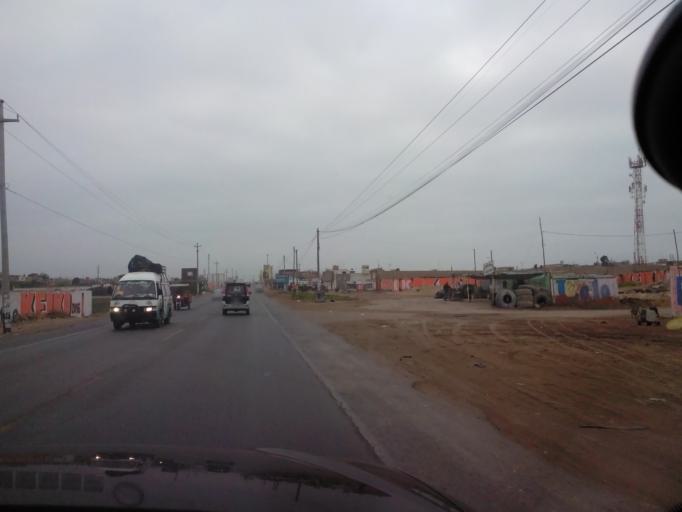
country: PE
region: Ica
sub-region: Provincia de Pisco
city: Villa Tupac Amaru
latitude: -13.7096
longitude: -76.1524
